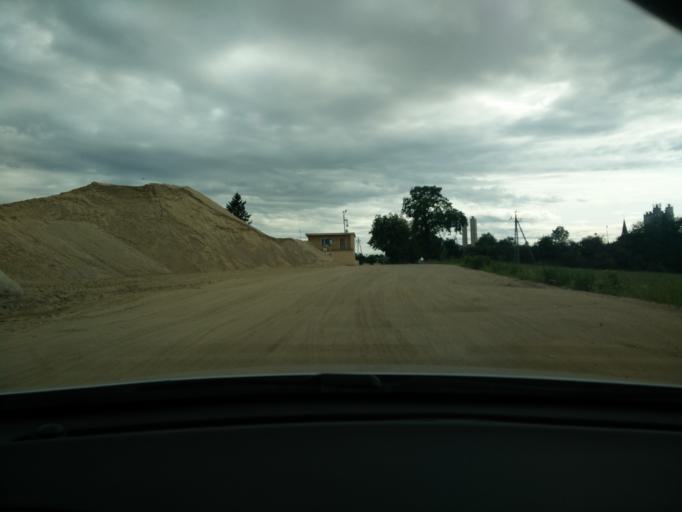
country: PL
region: Pomeranian Voivodeship
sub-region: Powiat pucki
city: Mrzezino
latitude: 54.6556
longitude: 18.4364
